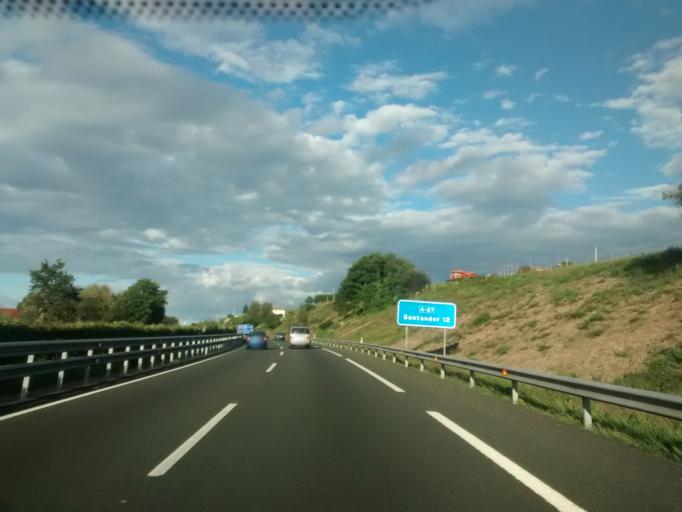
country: ES
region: Cantabria
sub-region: Provincia de Cantabria
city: Santa Cruz de Bezana
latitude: 43.4249
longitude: -3.9367
